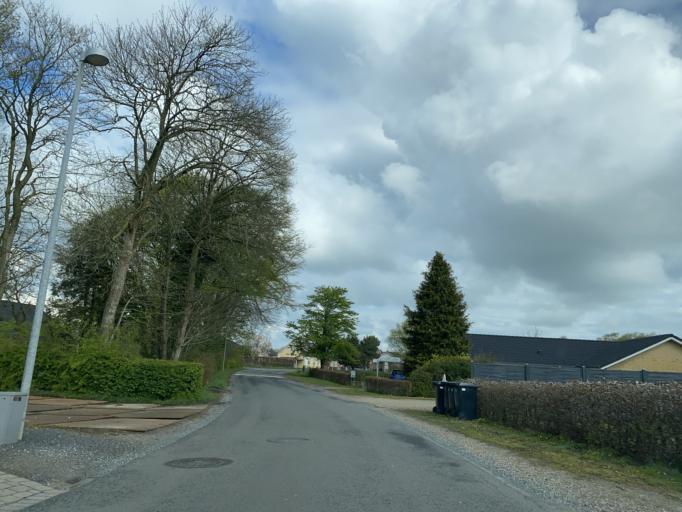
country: DK
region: Central Jutland
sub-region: Silkeborg Kommune
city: Silkeborg
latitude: 56.2152
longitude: 9.5178
